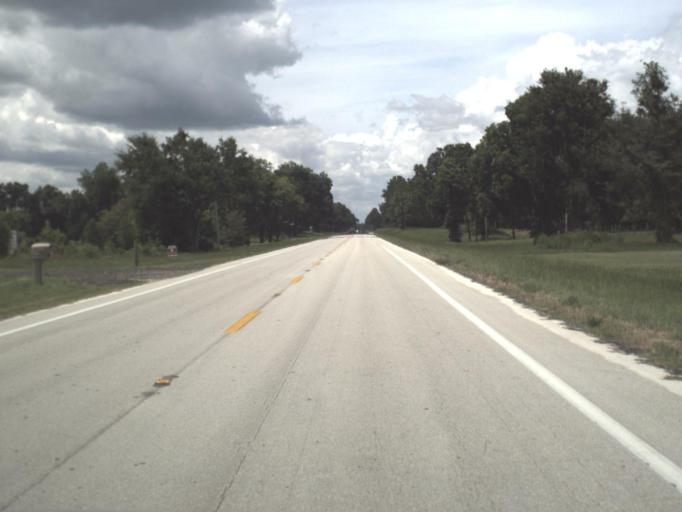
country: US
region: Florida
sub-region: Alachua County
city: High Springs
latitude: 29.7825
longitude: -82.6079
